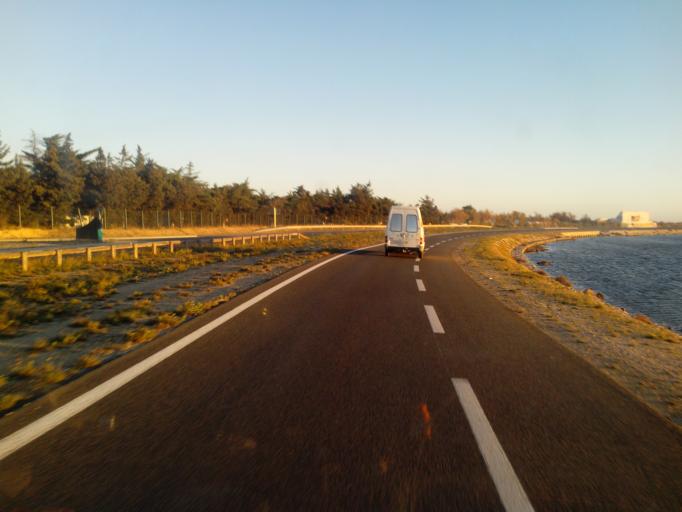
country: FR
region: Languedoc-Roussillon
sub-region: Departement de l'Aude
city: Leucate
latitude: 42.9032
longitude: 3.0477
